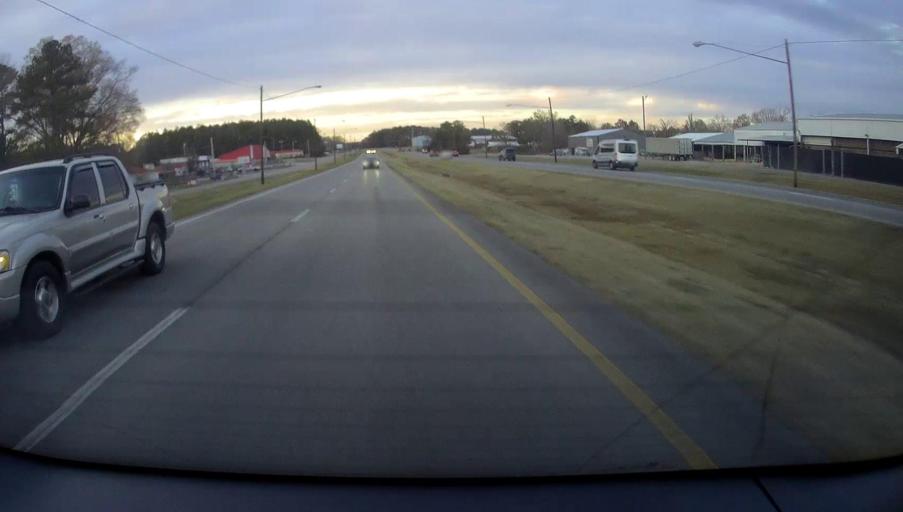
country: US
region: Alabama
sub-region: Etowah County
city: Glencoe
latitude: 33.9758
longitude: -85.9531
